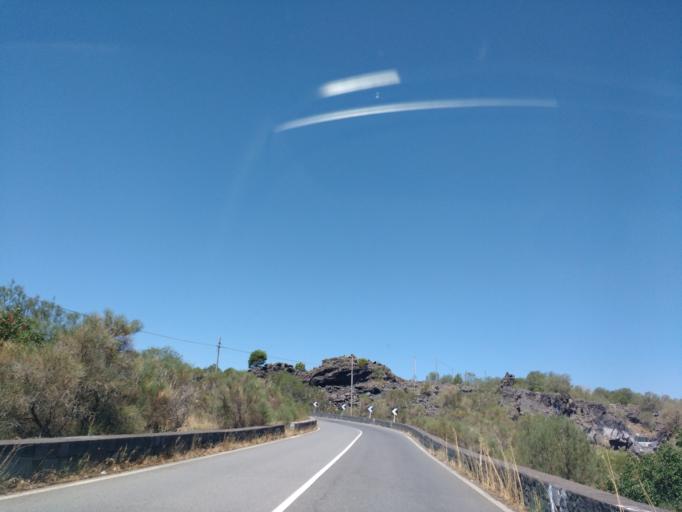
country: IT
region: Sicily
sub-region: Catania
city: Nicolosi
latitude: 37.6310
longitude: 15.0029
